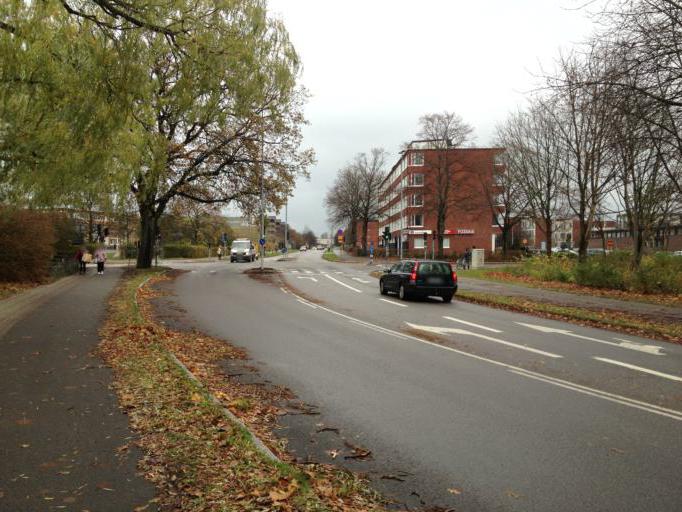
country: SE
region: Skane
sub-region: Lunds Kommun
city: Lund
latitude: 55.7087
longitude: 13.2111
